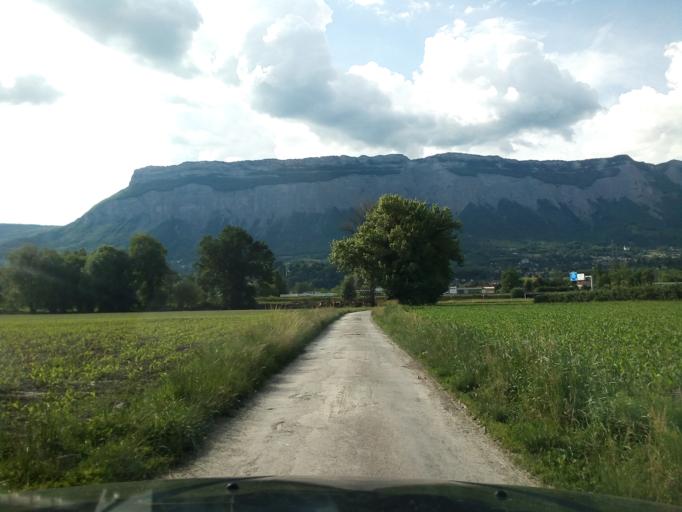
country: FR
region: Rhone-Alpes
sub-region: Departement de l'Isere
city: Montbonnot-Saint-Martin
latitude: 45.2149
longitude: 5.8177
